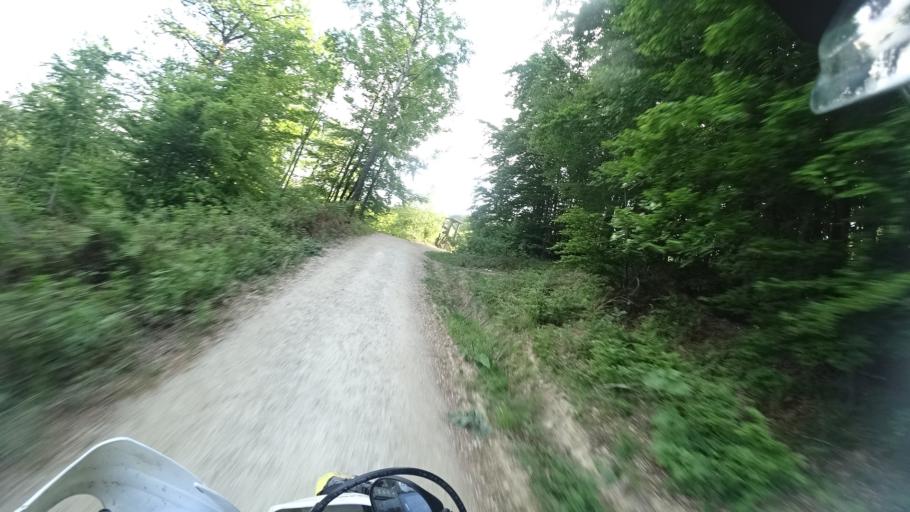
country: HR
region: Zagrebacka
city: Jablanovec
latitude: 45.8587
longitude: 15.8941
